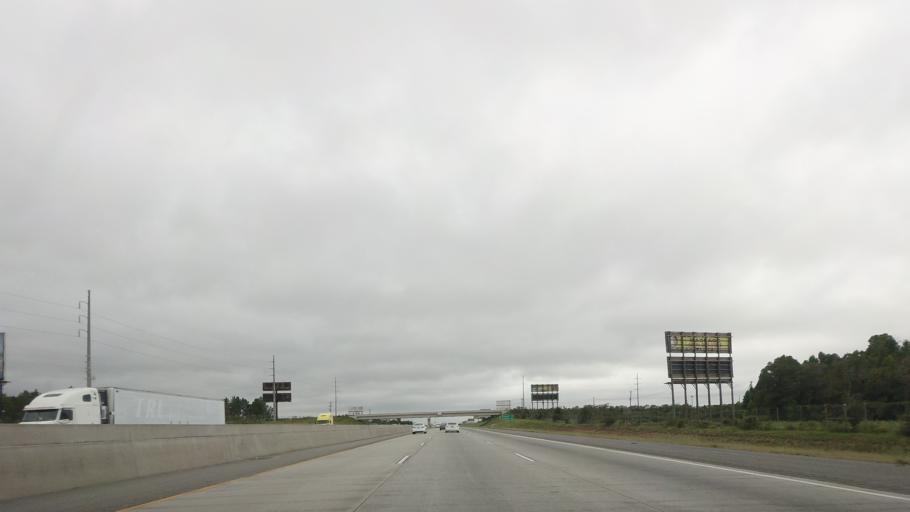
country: US
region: Georgia
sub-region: Tift County
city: Unionville
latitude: 31.4041
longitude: -83.5018
